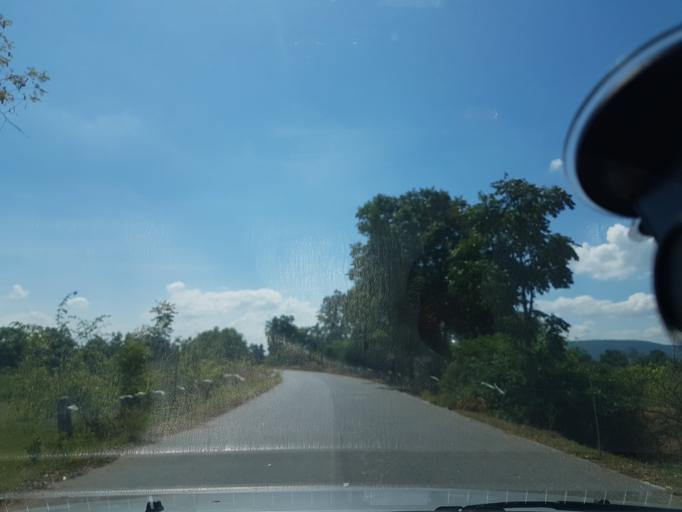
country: TH
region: Lop Buri
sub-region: Amphoe Tha Luang
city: Tha Luang
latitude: 14.9981
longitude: 101.0109
